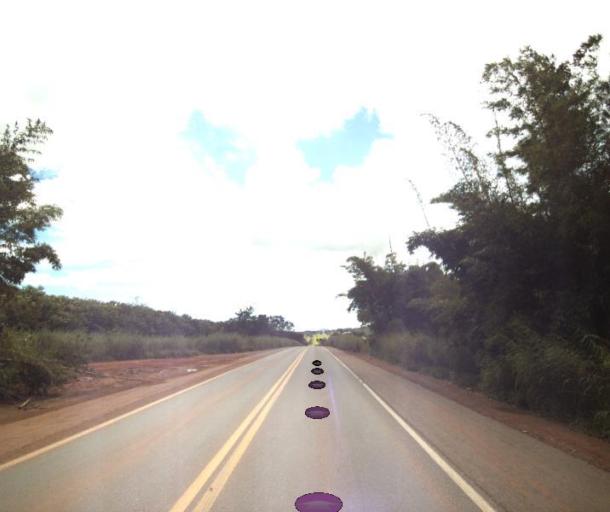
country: BR
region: Goias
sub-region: Petrolina De Goias
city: Petrolina de Goias
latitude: -15.9372
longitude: -49.2000
